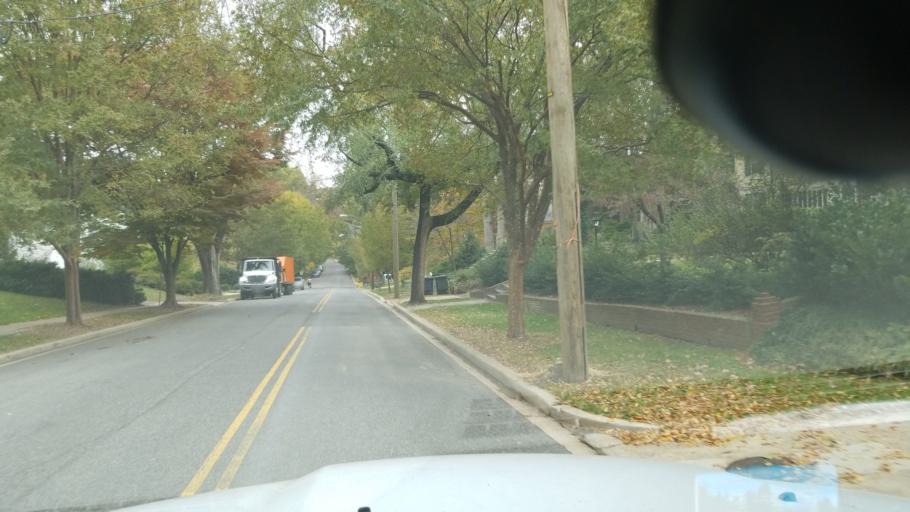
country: US
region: Maryland
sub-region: Montgomery County
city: Chevy Chase
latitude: 38.9479
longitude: -77.0594
